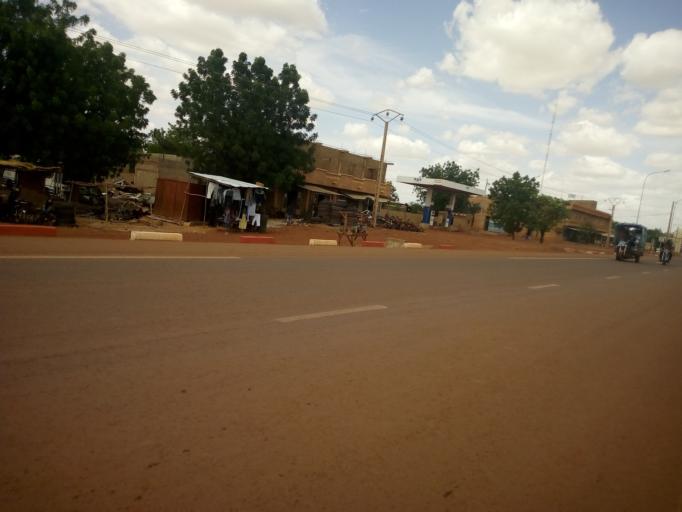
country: ML
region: Segou
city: Segou
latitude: 13.4341
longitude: -6.2310
